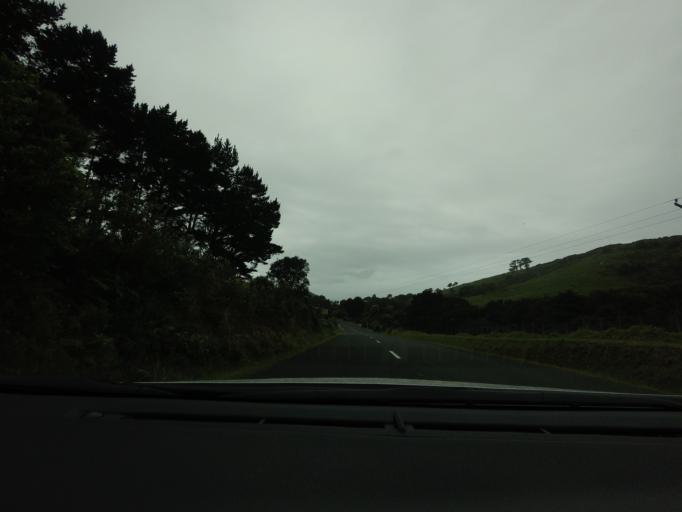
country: NZ
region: Auckland
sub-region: Auckland
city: Warkworth
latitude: -36.2741
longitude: 174.7940
